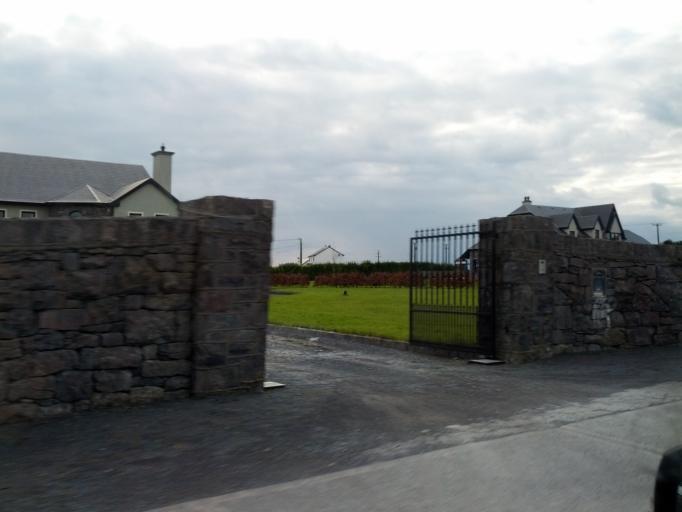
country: IE
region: Connaught
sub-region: County Galway
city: Athenry
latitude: 53.3755
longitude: -8.7086
